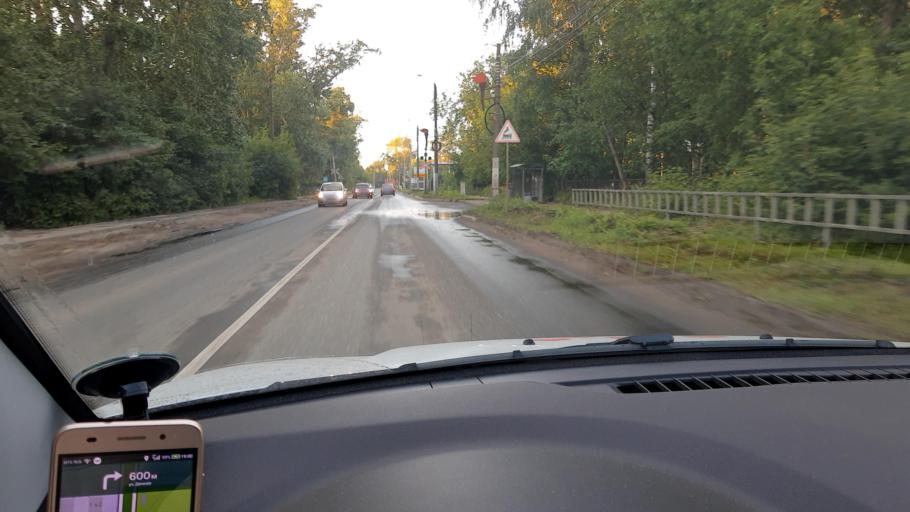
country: RU
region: Nizjnij Novgorod
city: Nizhniy Novgorod
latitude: 56.2940
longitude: 43.9104
